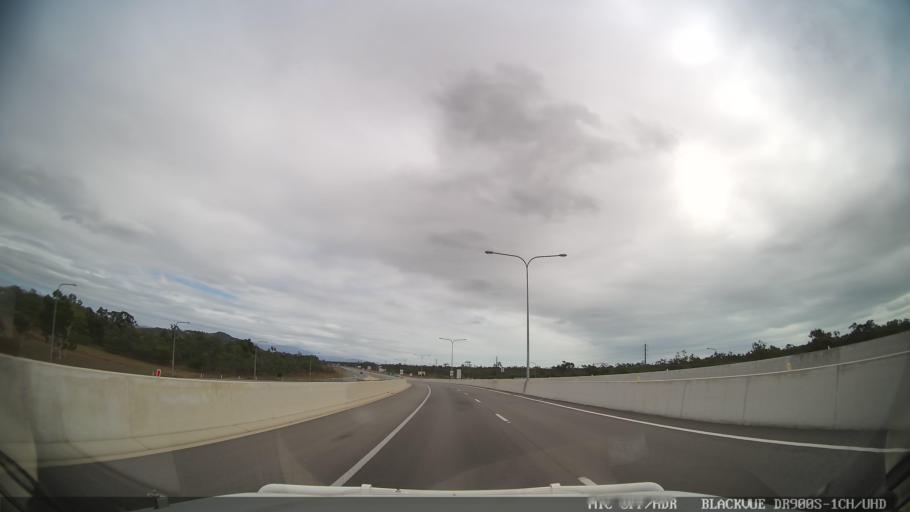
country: AU
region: Queensland
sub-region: Townsville
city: Bohle Plains
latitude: -19.2402
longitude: 146.6629
